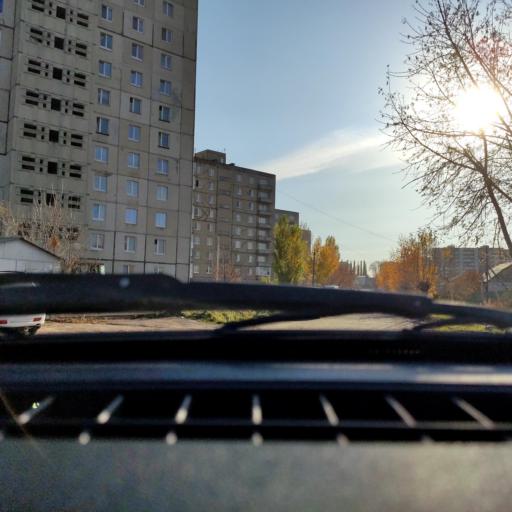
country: RU
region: Bashkortostan
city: Ufa
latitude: 54.8226
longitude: 56.1256
